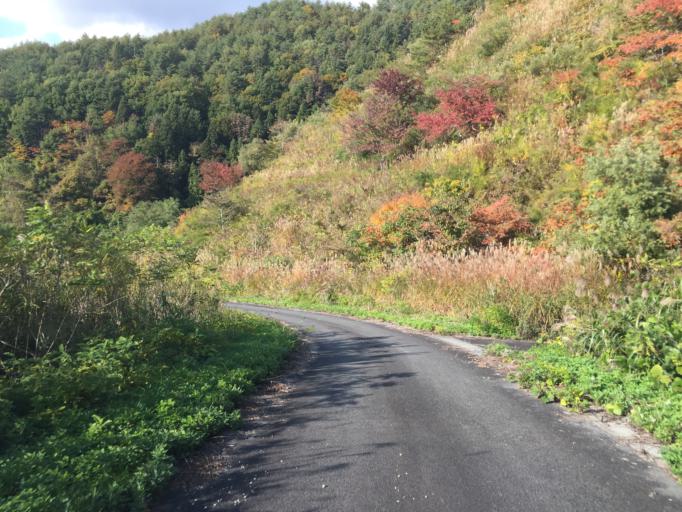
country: JP
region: Fukushima
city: Kitakata
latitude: 37.7528
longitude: 139.9178
